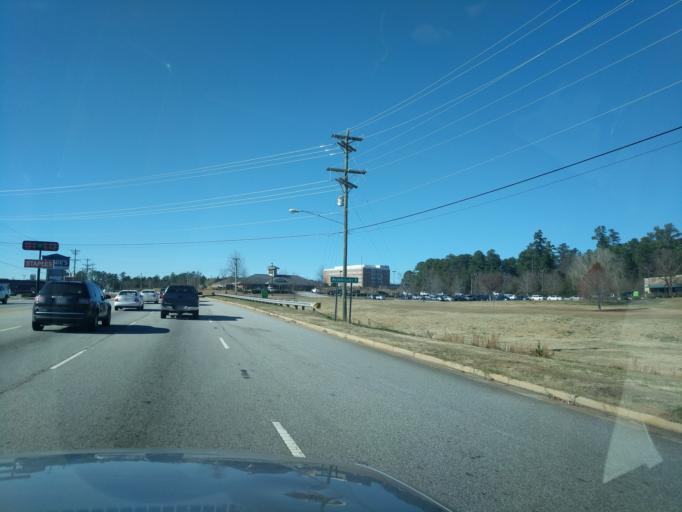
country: US
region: South Carolina
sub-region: Oconee County
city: Seneca
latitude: 34.6932
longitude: -82.9803
